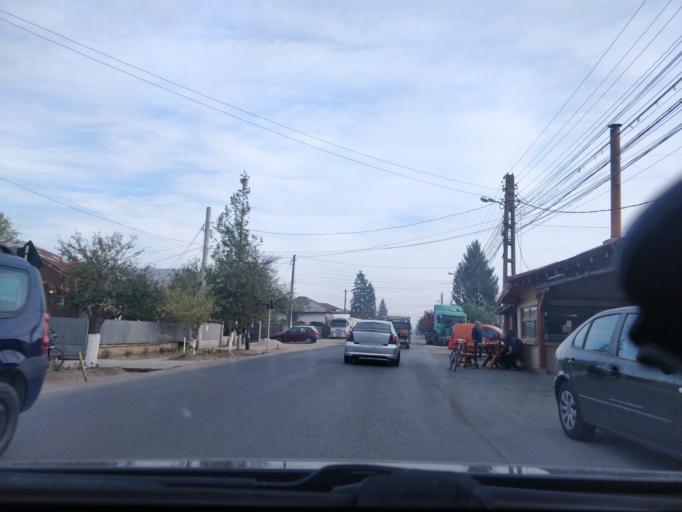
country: RO
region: Giurgiu
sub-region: Comuna Bolintin Vale
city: Malu Spart
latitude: 44.4423
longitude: 25.7162
